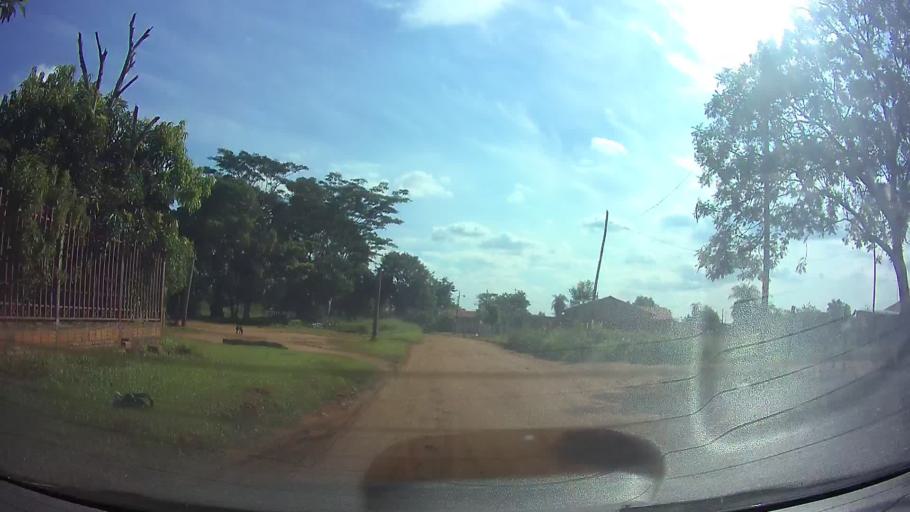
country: PY
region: Central
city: Limpio
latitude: -25.2408
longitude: -57.4654
